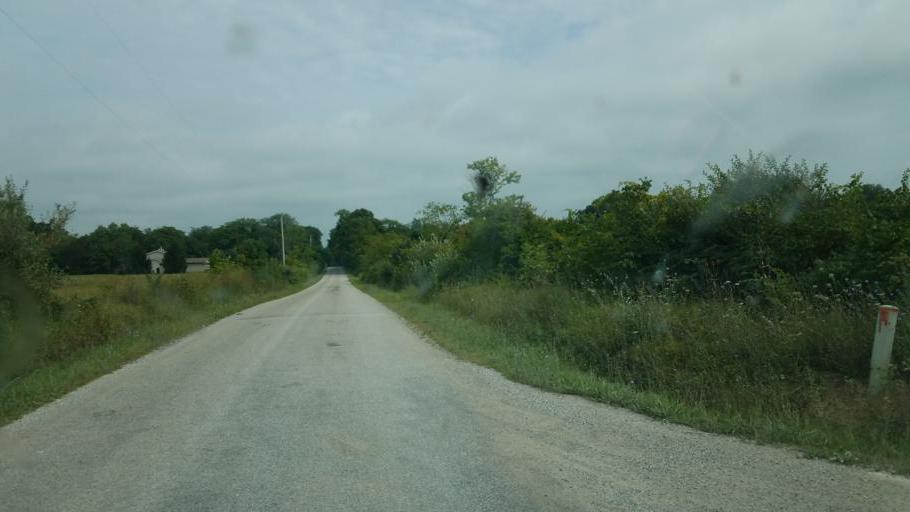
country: US
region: Ohio
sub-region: Morrow County
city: Cardington
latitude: 40.4087
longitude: -82.8520
